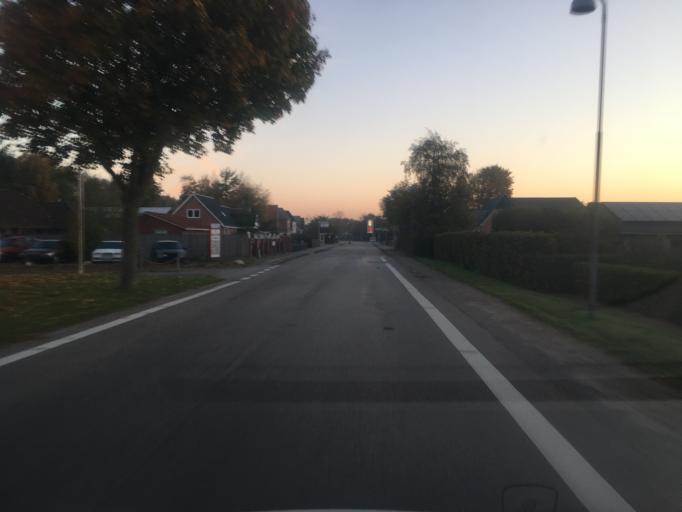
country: DE
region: Schleswig-Holstein
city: Bramstedtlund
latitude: 54.9385
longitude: 9.0816
